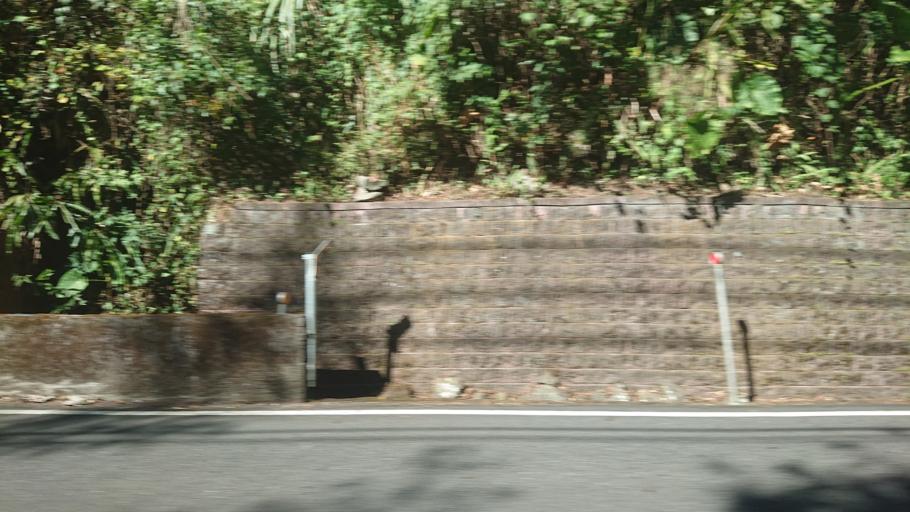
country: TW
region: Taiwan
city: Lugu
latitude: 23.4868
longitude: 120.7526
